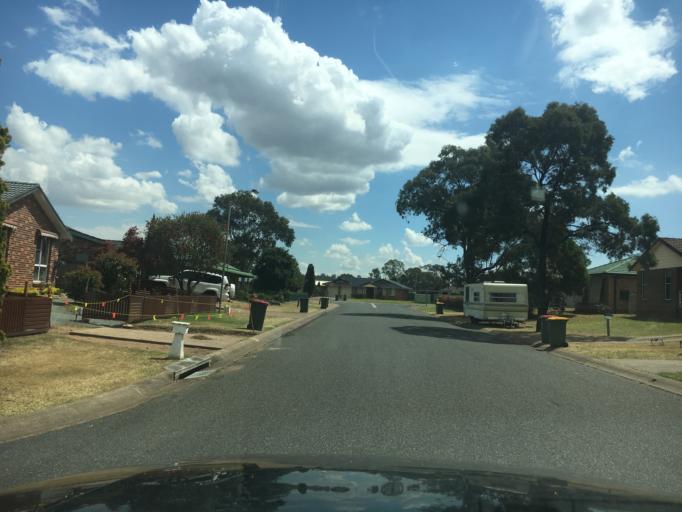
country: AU
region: New South Wales
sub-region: Singleton
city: Singleton
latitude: -32.5460
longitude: 151.1729
